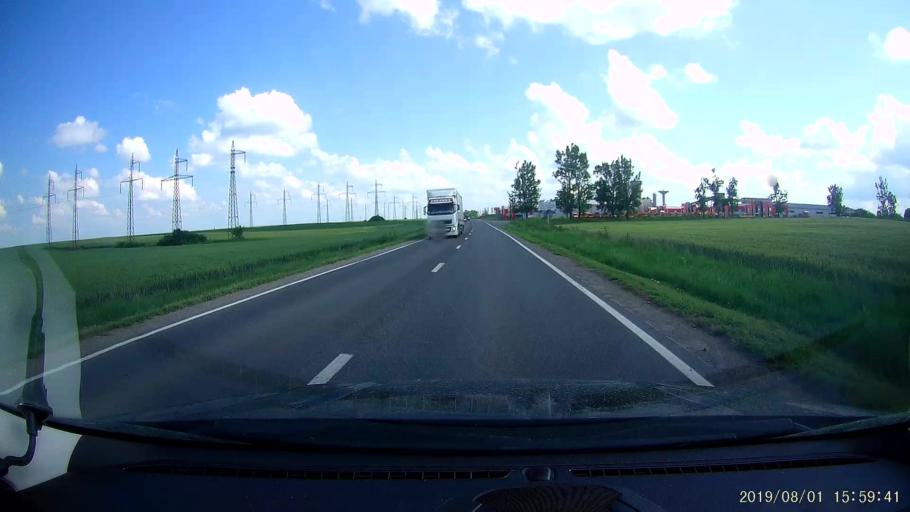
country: RO
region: Ialomita
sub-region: Comuna Slobozia
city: Slobozia
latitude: 44.5433
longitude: 27.3849
